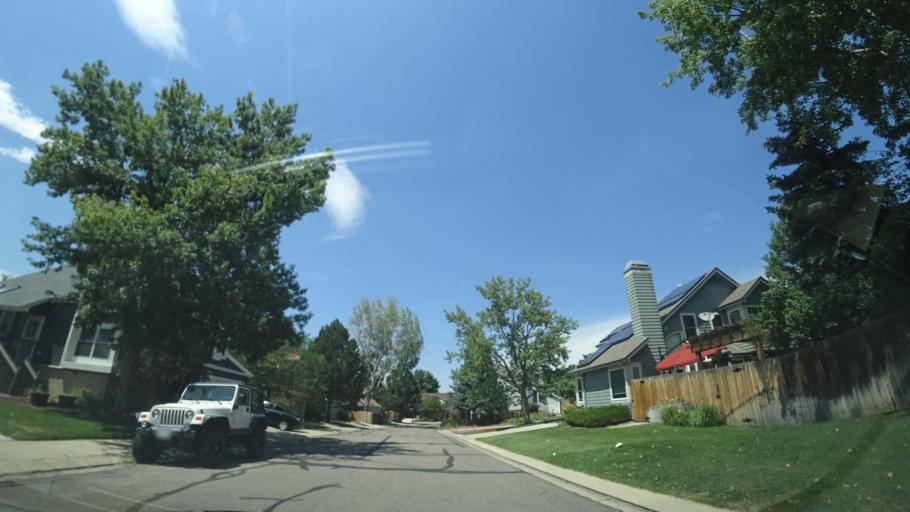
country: US
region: Colorado
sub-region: Jefferson County
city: Lakewood
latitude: 39.6947
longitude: -105.0980
